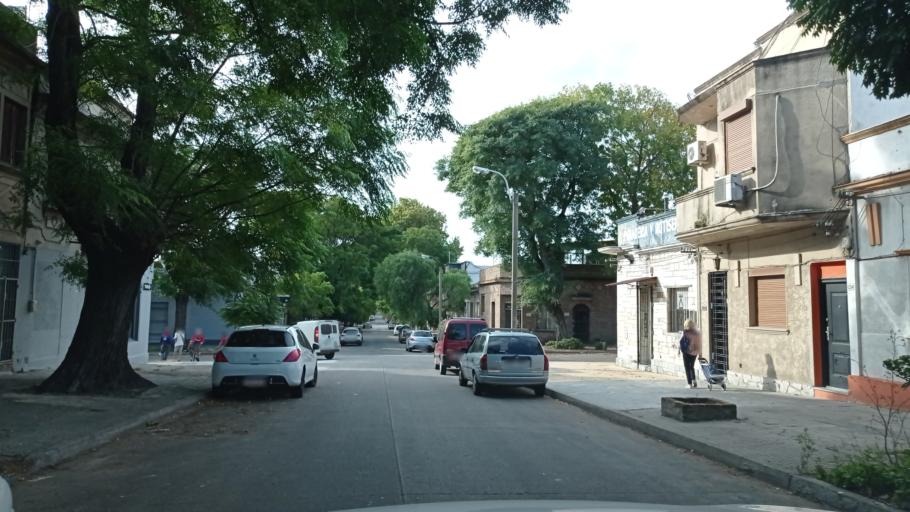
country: UY
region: Montevideo
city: Montevideo
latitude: -34.8838
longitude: -56.1754
